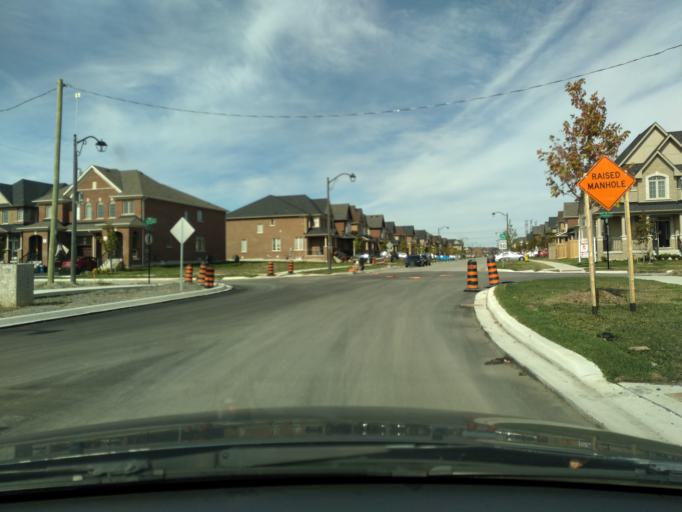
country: CA
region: Ontario
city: Oshawa
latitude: 43.9537
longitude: -78.9113
